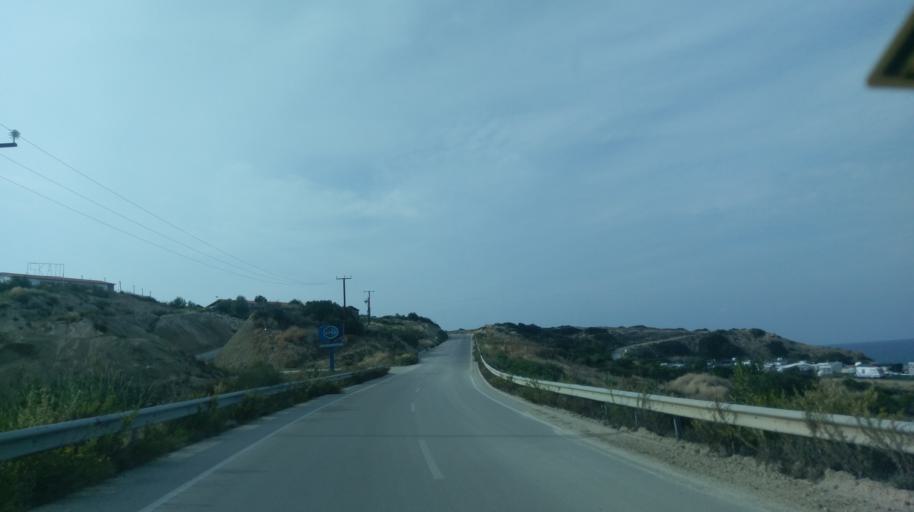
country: CY
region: Ammochostos
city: Trikomo
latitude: 35.4236
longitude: 33.8983
